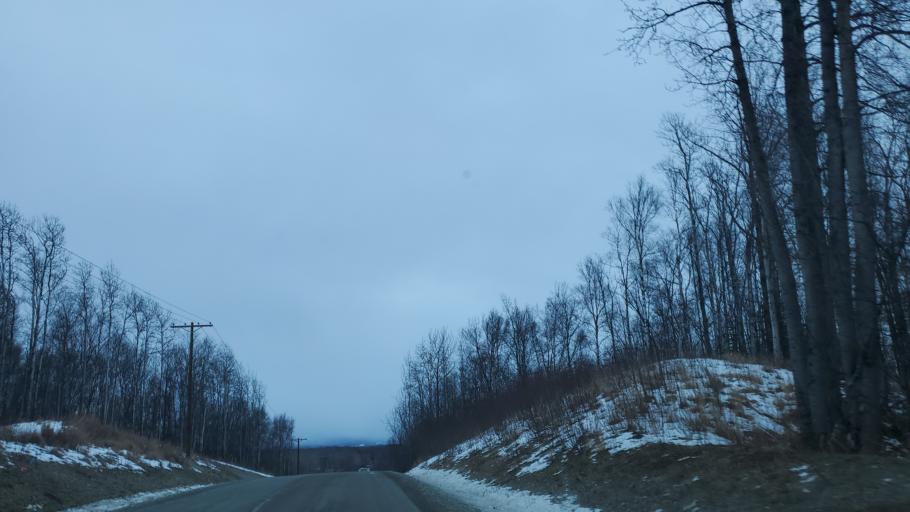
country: US
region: Alaska
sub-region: Matanuska-Susitna Borough
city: Gateway
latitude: 61.6572
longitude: -149.2278
